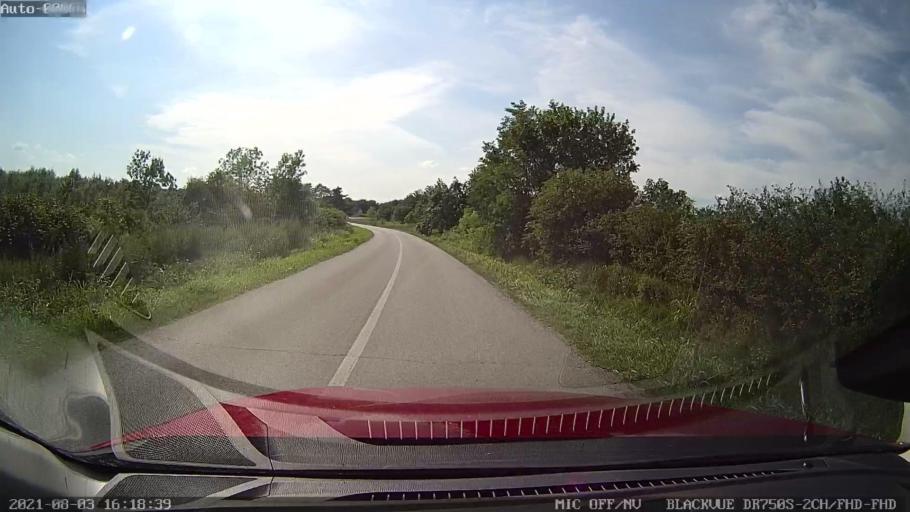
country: HR
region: Osjecko-Baranjska
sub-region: Grad Osijek
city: Bilje
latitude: 45.6082
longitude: 18.7595
